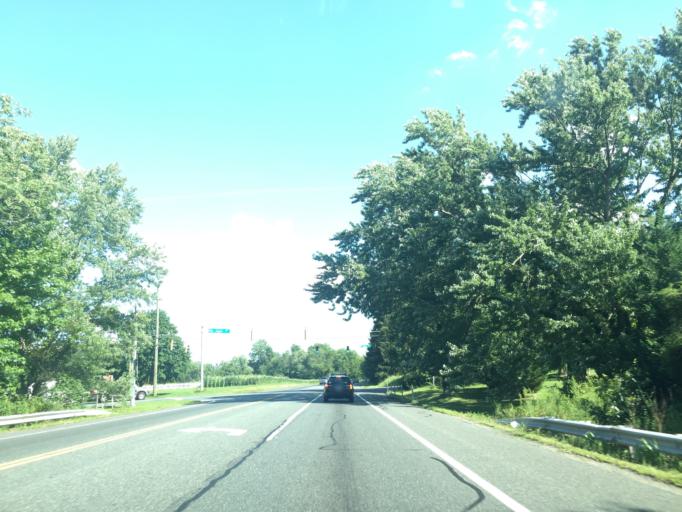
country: US
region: Maryland
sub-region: Harford County
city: Pleasant Hills
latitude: 39.4765
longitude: -76.3805
